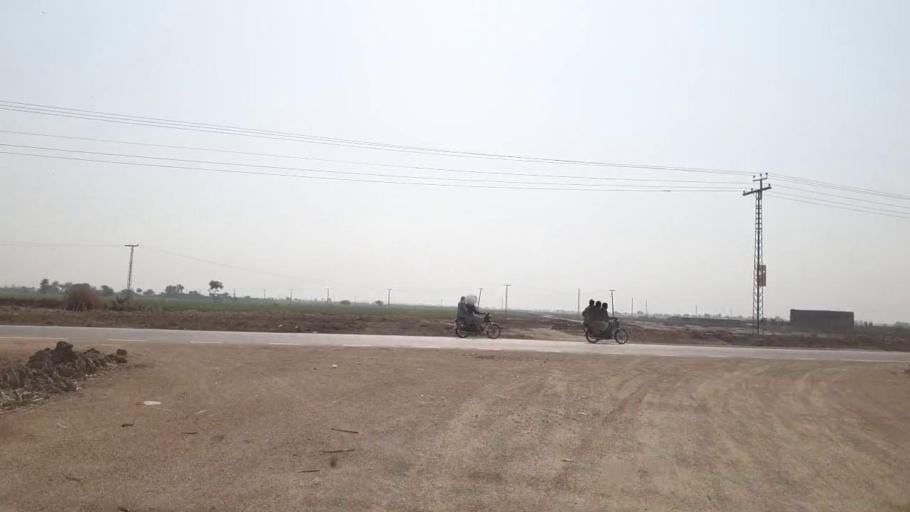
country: PK
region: Sindh
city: Mirpur Khas
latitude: 25.5523
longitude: 69.0491
